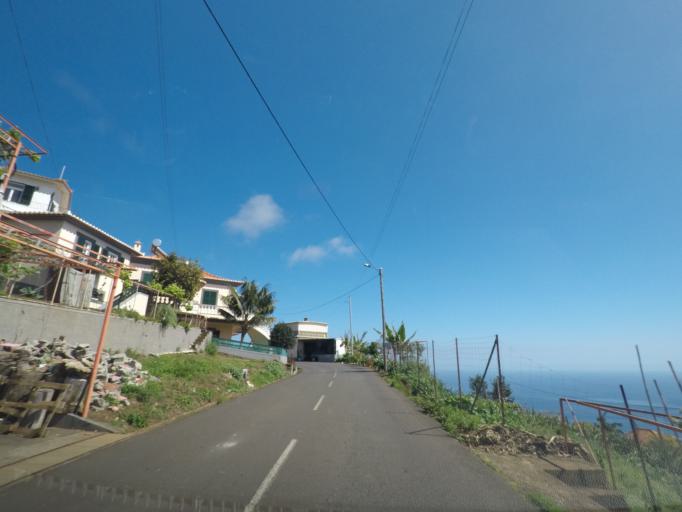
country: PT
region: Madeira
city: Ponta do Sol
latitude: 32.6956
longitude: -17.0995
